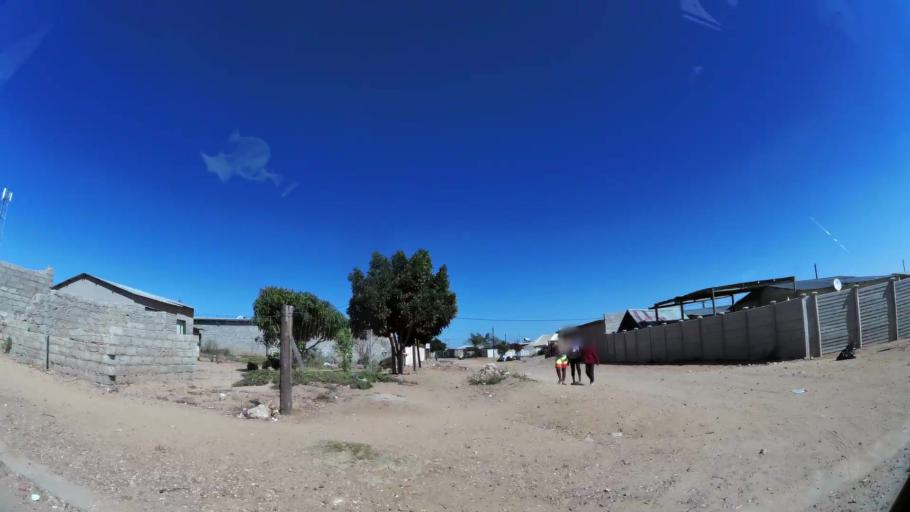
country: ZA
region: Limpopo
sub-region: Capricorn District Municipality
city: Polokwane
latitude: -23.8743
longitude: 29.4105
